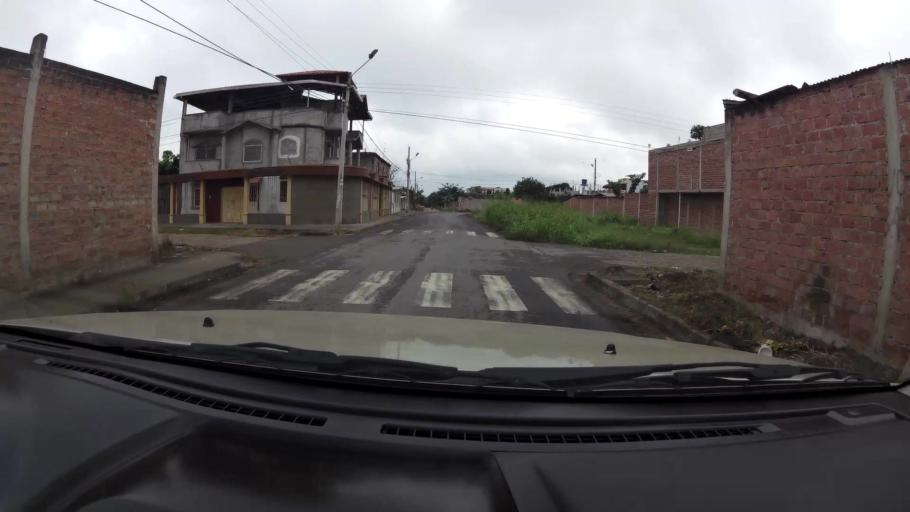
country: EC
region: El Oro
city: Pasaje
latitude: -3.3263
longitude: -79.8252
